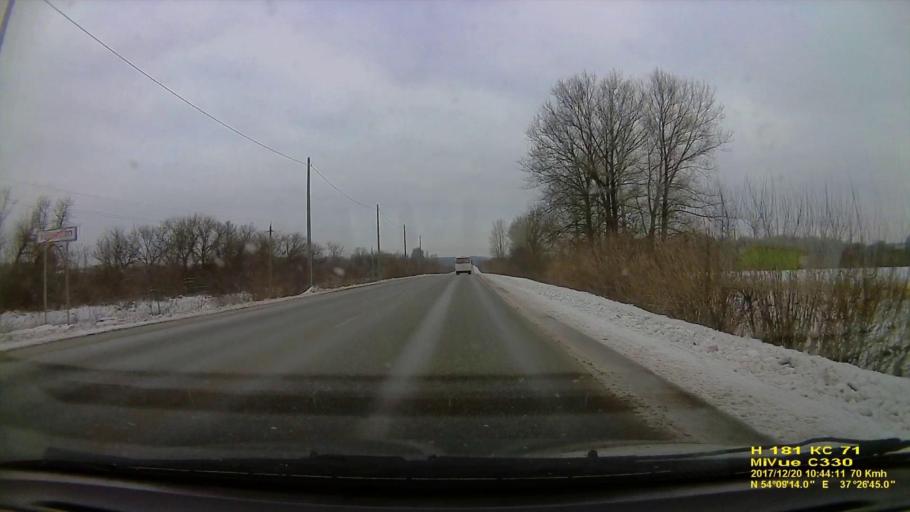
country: RU
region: Tula
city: Kosaya Gora
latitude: 54.1540
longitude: 37.4460
